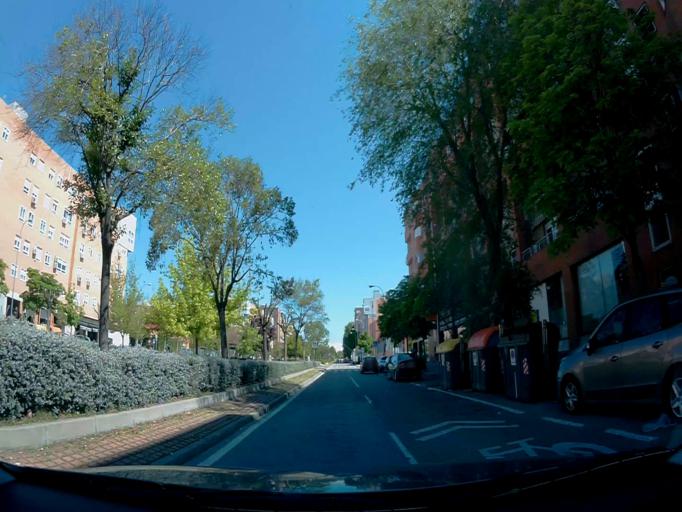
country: ES
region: Madrid
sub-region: Provincia de Madrid
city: Vicalvaro
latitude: 40.4010
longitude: -3.6210
